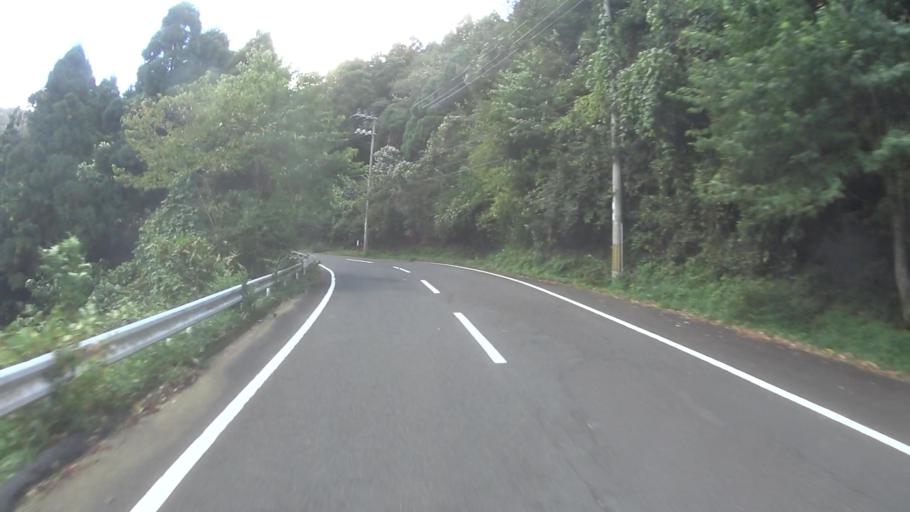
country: JP
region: Kyoto
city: Maizuru
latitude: 35.5435
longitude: 135.3965
